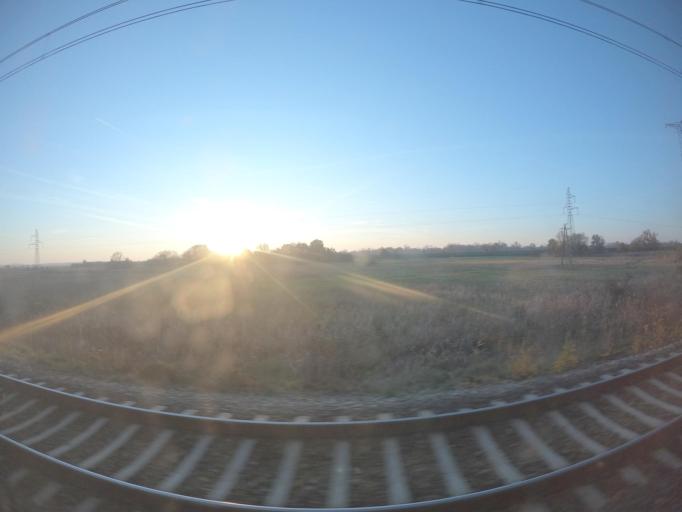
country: PL
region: Lubusz
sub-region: Powiat gorzowski
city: Kostrzyn nad Odra
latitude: 52.5674
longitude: 14.6462
